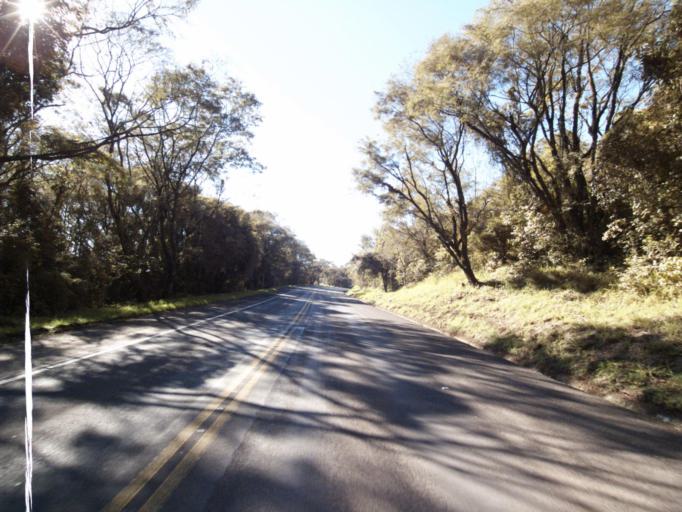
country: BR
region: Rio Grande do Sul
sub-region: Frederico Westphalen
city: Frederico Westphalen
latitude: -26.7931
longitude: -53.4537
